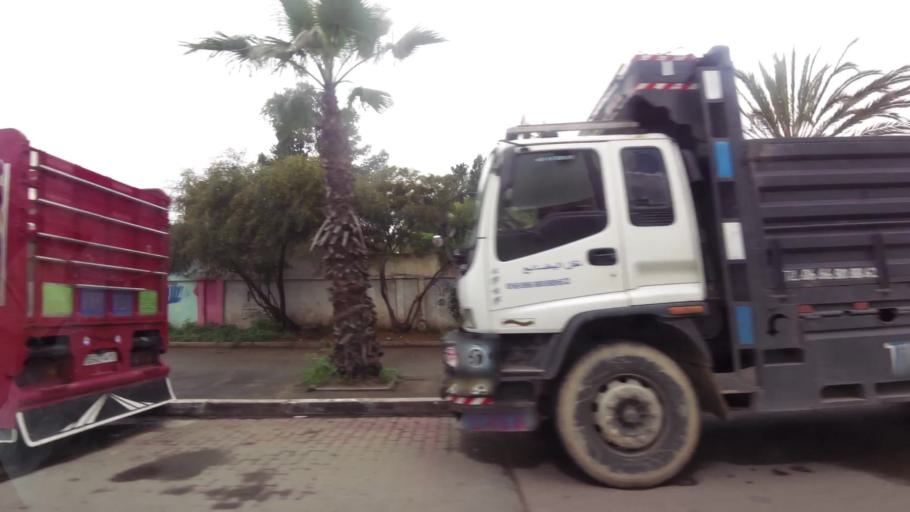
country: MA
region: Grand Casablanca
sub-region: Nouaceur
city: Bouskoura
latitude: 33.5107
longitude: -7.6568
